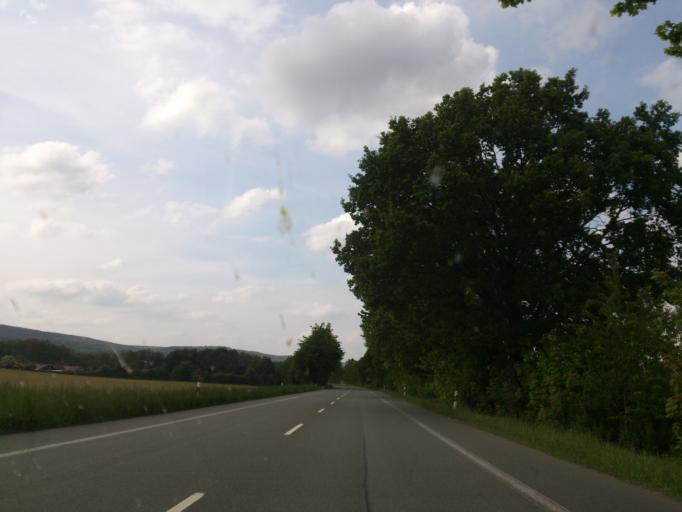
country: DE
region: North Rhine-Westphalia
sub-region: Regierungsbezirk Detmold
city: Willebadessen
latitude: 51.6166
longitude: 9.0330
